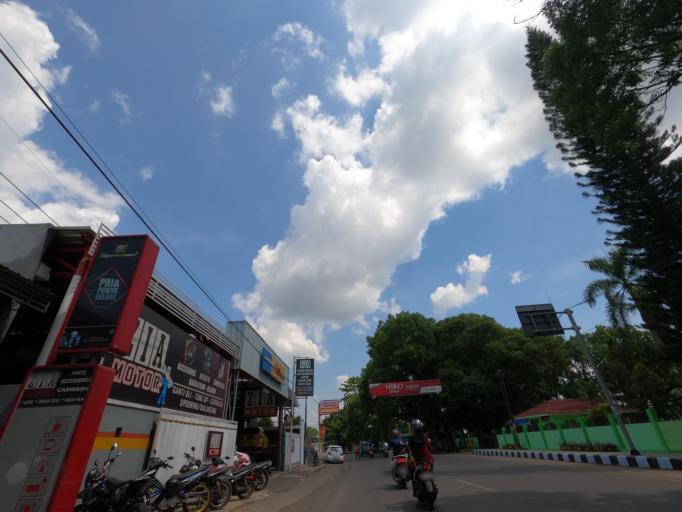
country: ID
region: West Java
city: Pamanukan
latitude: -6.5524
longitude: 107.7540
